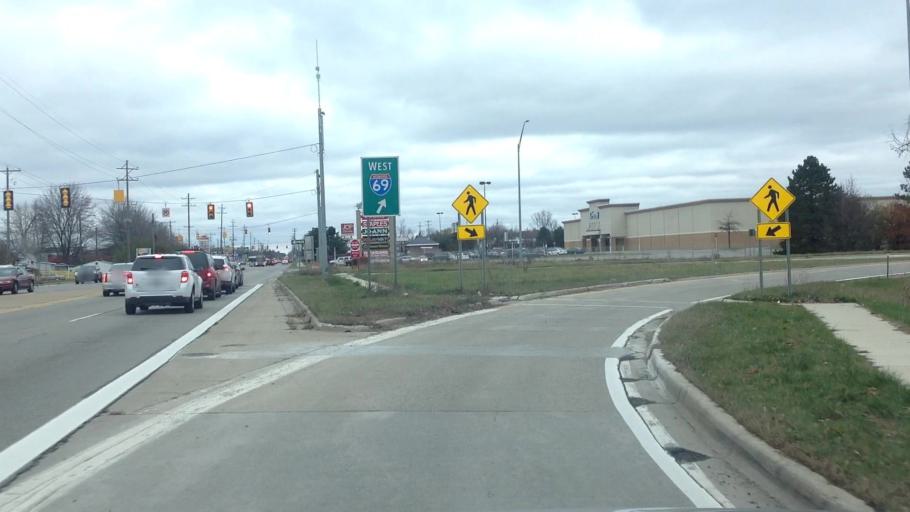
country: US
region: Michigan
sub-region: Genesee County
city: Burton
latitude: 43.0148
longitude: -83.6347
